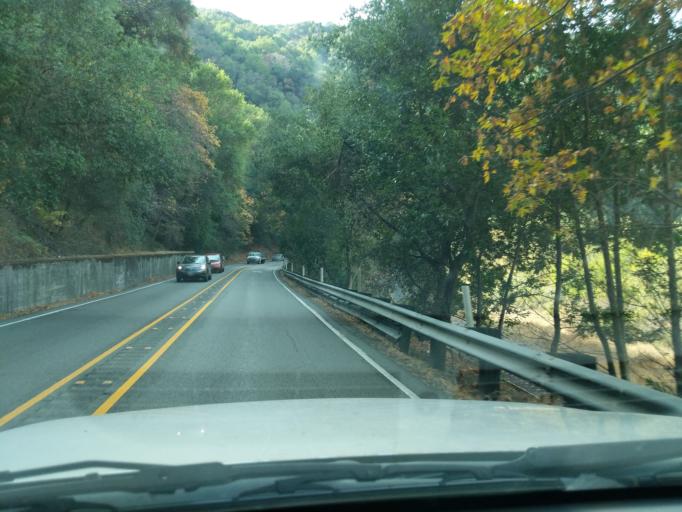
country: US
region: California
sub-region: Alameda County
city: Fremont
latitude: 37.5914
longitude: -121.9337
